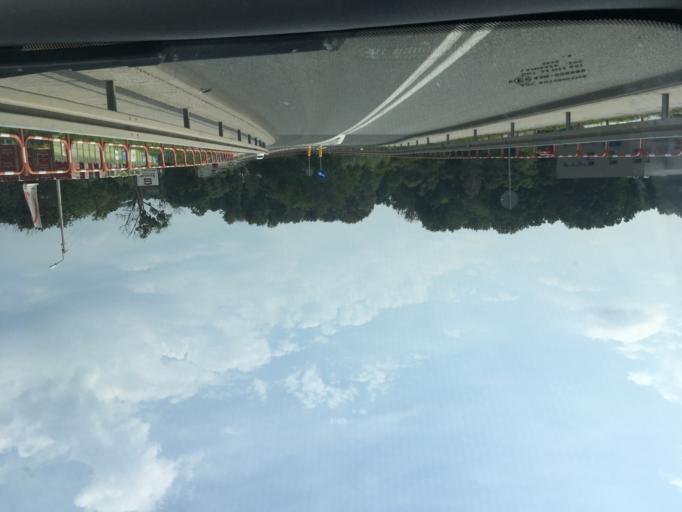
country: PL
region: Silesian Voivodeship
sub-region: Powiat rybnicki
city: Stanowice
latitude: 50.1307
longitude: 18.6907
